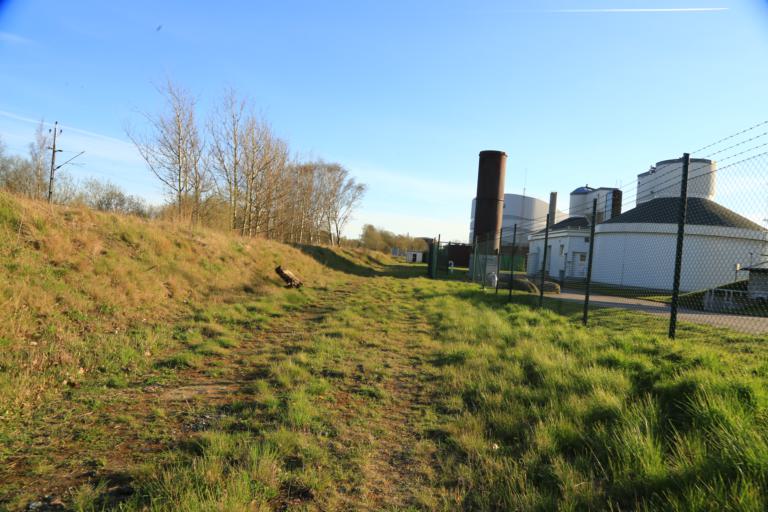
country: SE
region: Halland
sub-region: Varbergs Kommun
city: Varberg
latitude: 57.1222
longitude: 12.2553
